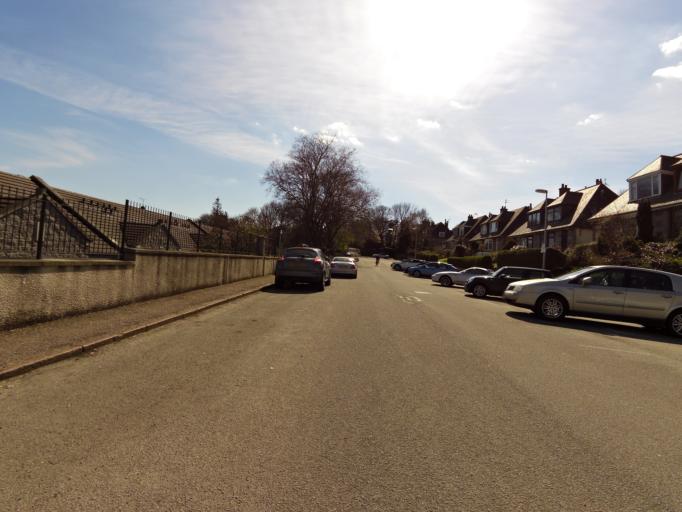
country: GB
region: Scotland
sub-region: Aberdeen City
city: Aberdeen
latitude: 57.1369
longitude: -2.0988
